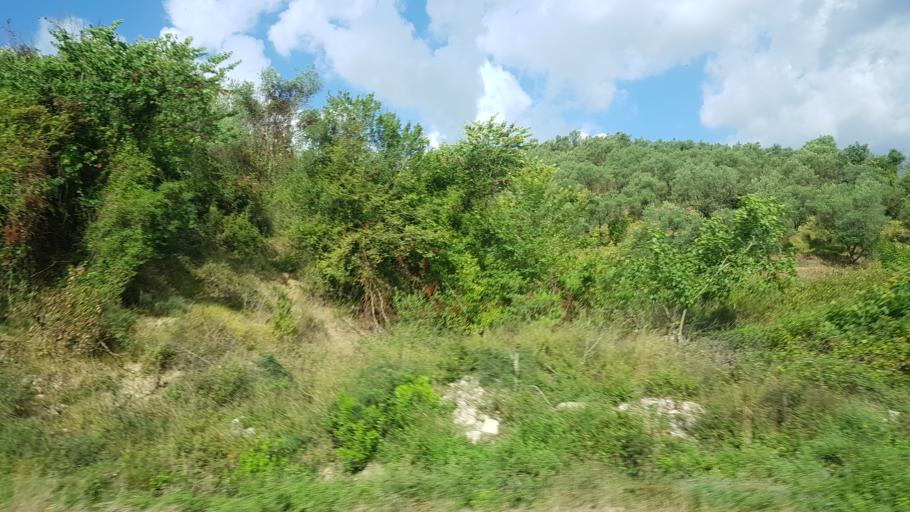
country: AL
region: Vlore
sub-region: Rrethi i Delvines
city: Mesopotam
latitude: 39.9037
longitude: 20.0847
